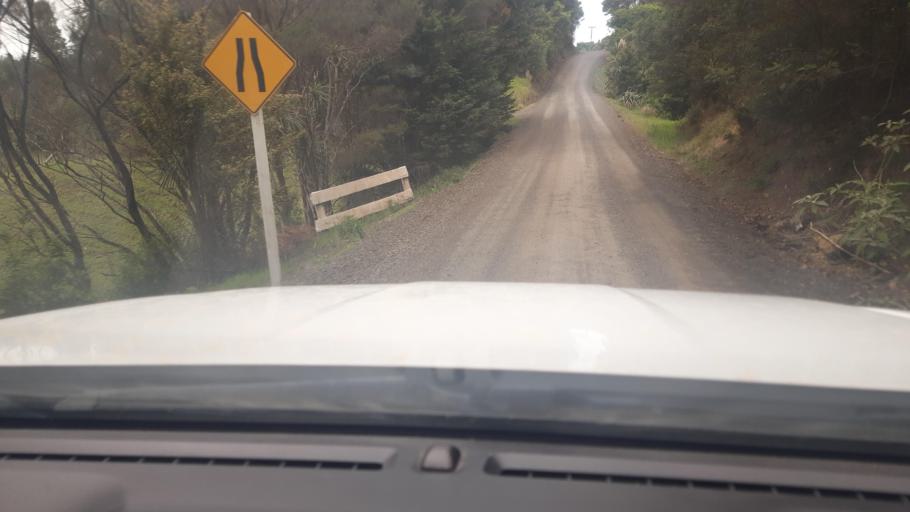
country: NZ
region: Northland
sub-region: Far North District
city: Kaitaia
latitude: -35.0759
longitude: 173.3220
